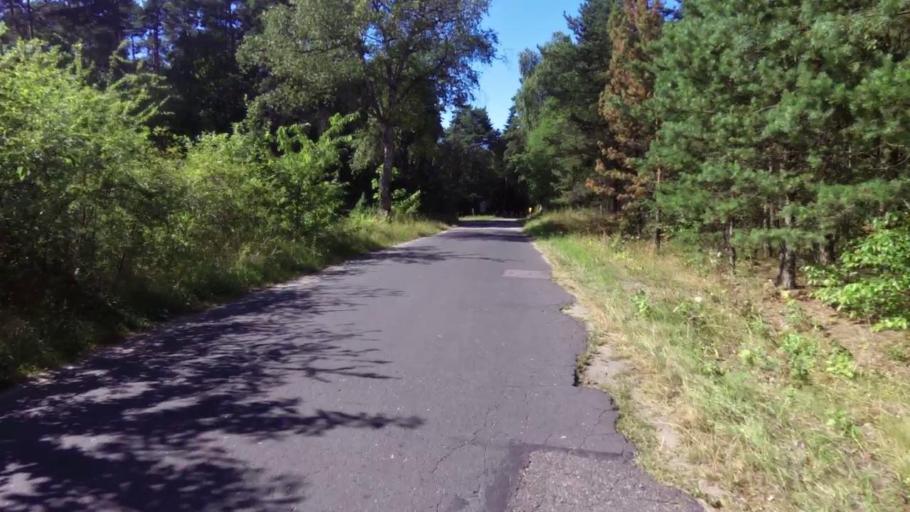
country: PL
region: West Pomeranian Voivodeship
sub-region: Powiat szczecinecki
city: Borne Sulinowo
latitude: 53.5756
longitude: 16.5682
